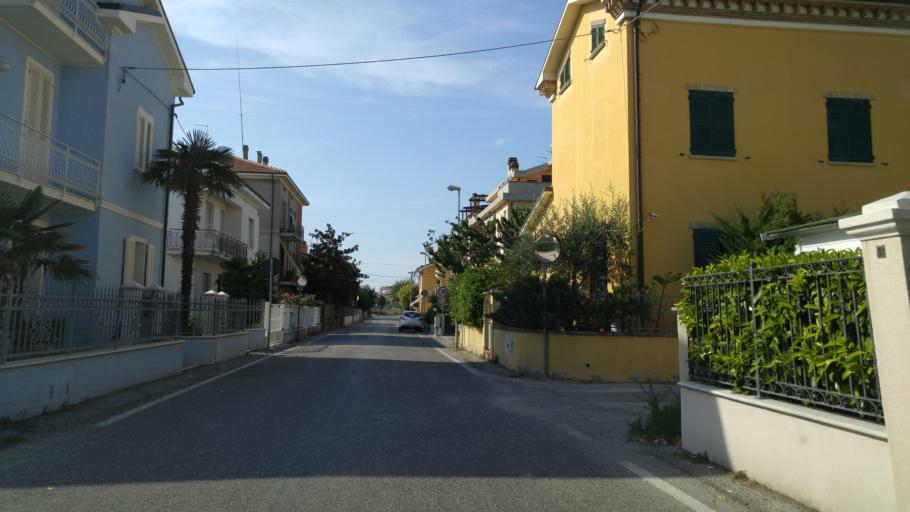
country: IT
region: The Marches
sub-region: Provincia di Pesaro e Urbino
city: Pesaro
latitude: 43.8986
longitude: 12.9151
